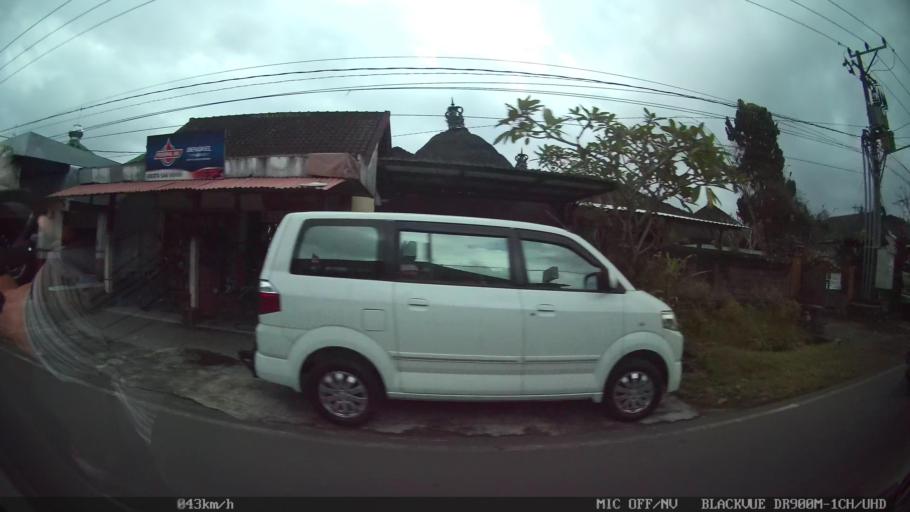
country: ID
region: Bali
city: Penebel
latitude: -8.4251
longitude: 115.1444
